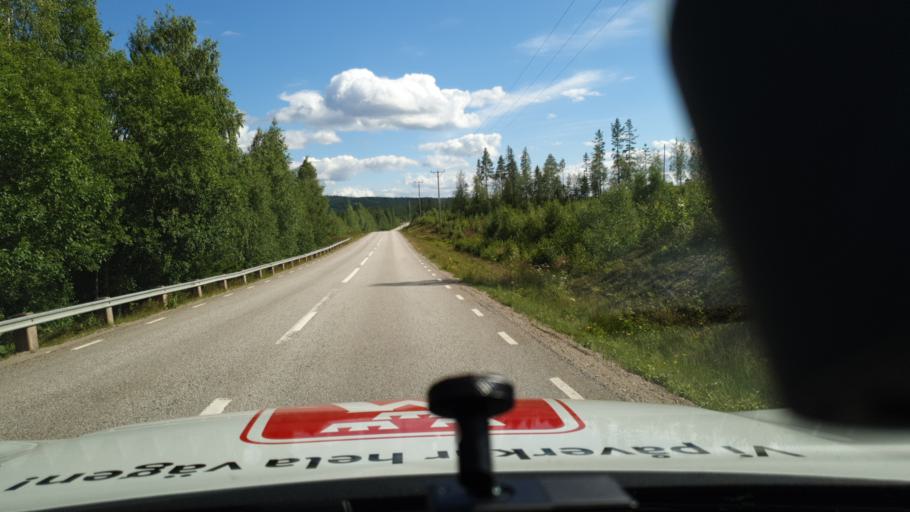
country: NO
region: Hedmark
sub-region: Trysil
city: Innbygda
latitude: 60.9987
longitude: 12.4883
